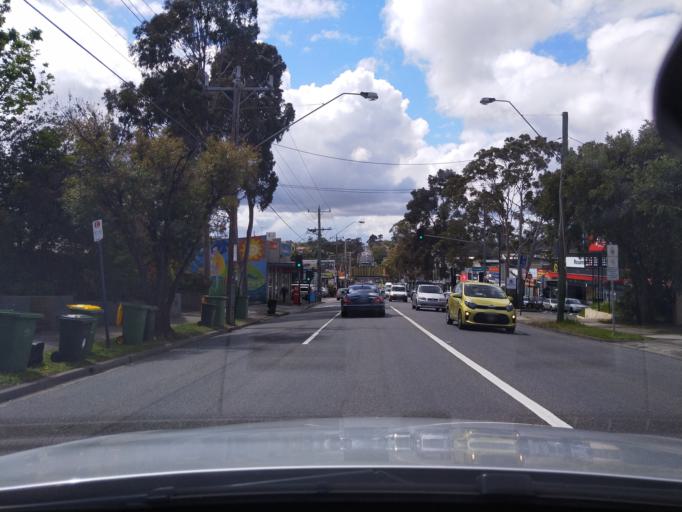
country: AU
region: Victoria
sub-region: Banyule
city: Heidelberg Heights
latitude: -37.7435
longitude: 145.0638
